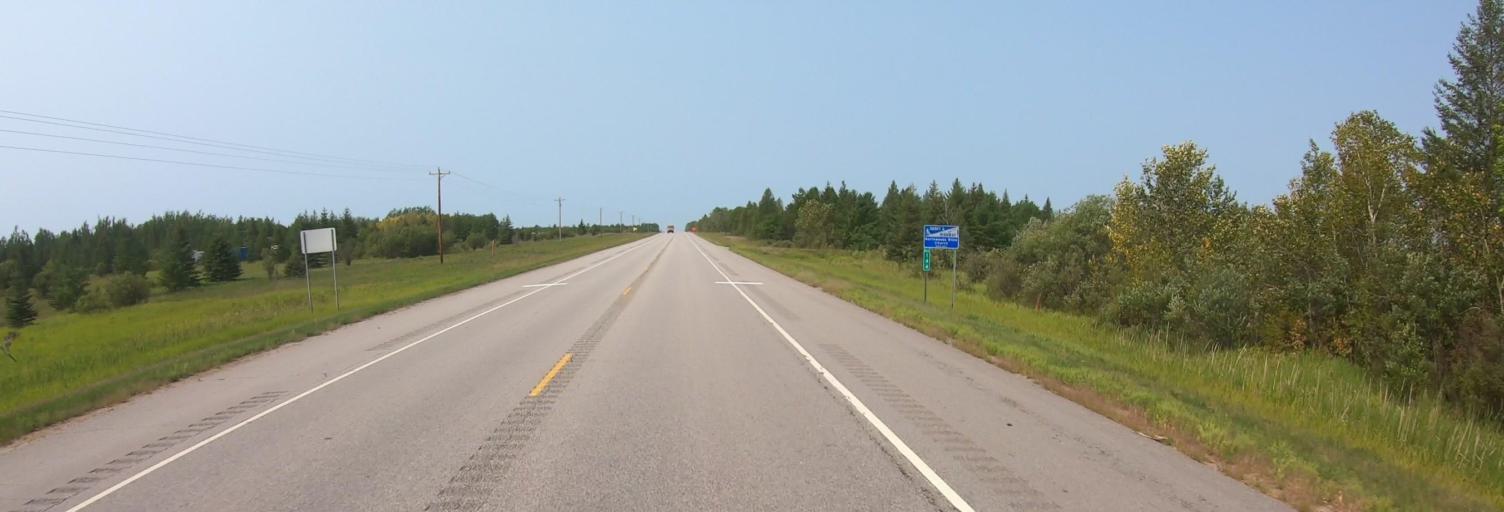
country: CA
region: Ontario
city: Fort Frances
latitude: 48.4102
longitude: -93.1532
